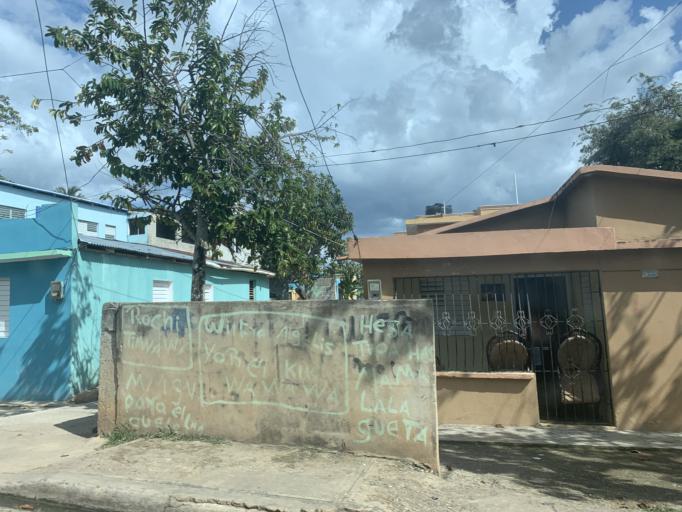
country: DO
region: Monte Plata
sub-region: Yamasa
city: Yamasa
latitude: 18.7741
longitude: -70.0299
